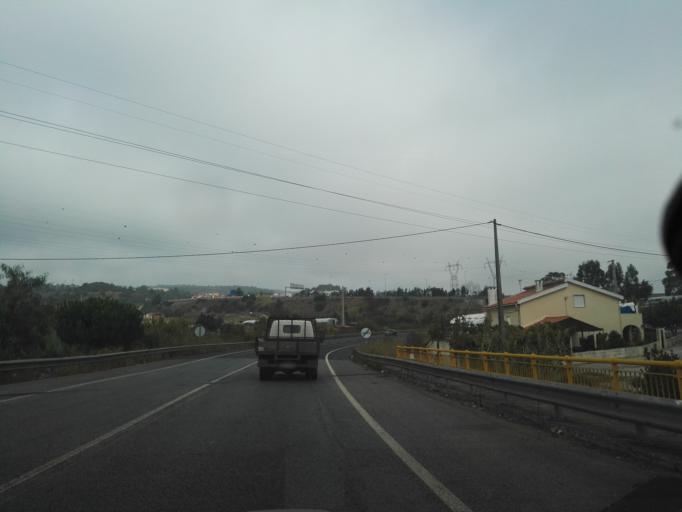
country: PT
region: Lisbon
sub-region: Vila Franca de Xira
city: Vialonga
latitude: 38.8932
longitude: -9.0520
